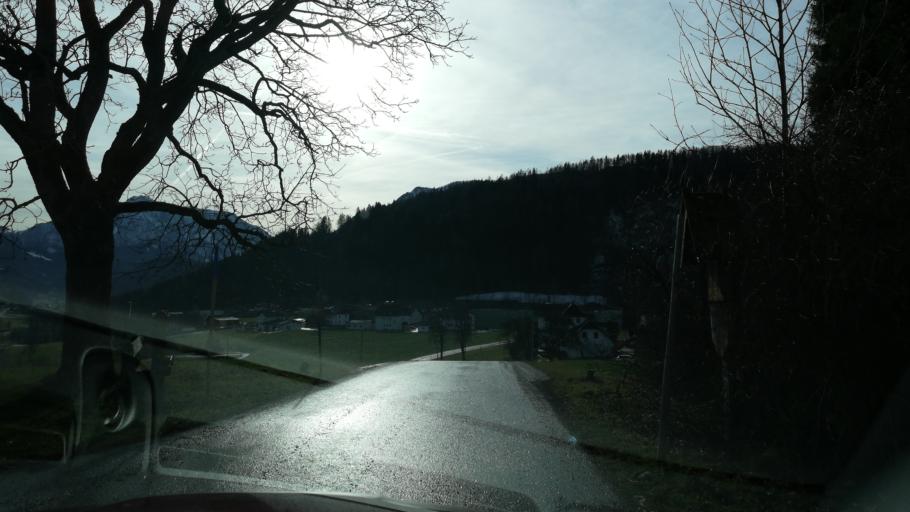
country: AT
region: Upper Austria
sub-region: Politischer Bezirk Kirchdorf an der Krems
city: Rossleithen
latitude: 47.7138
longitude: 14.3424
